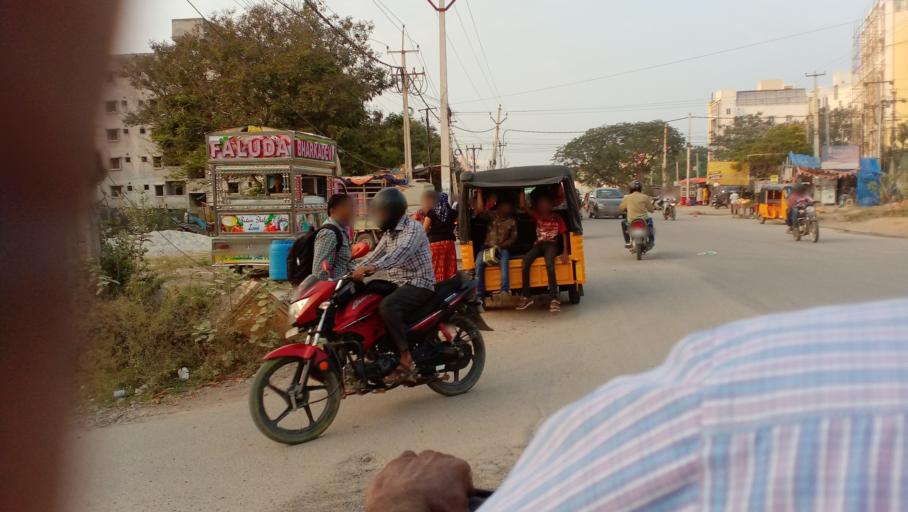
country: IN
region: Telangana
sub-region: Medak
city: Serilingampalle
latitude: 17.5041
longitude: 78.3181
